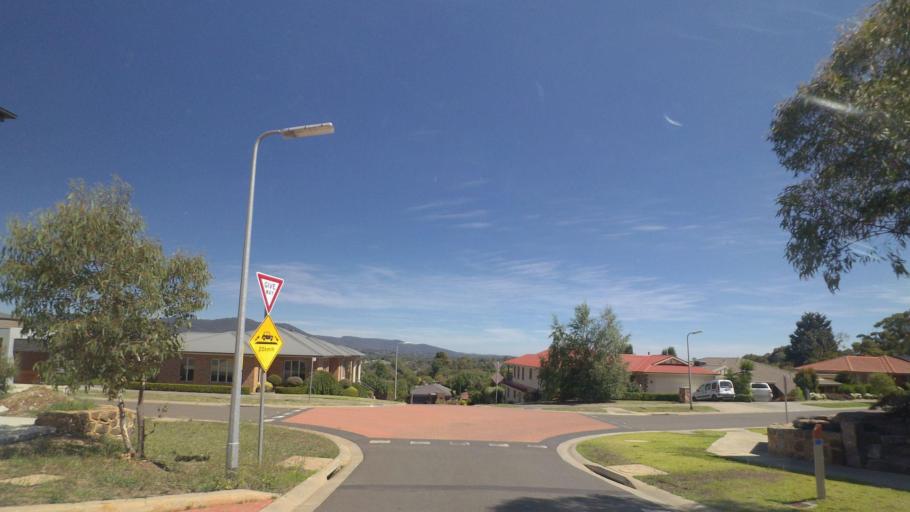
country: AU
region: Victoria
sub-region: Yarra Ranges
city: Lilydale
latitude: -37.7620
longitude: 145.3286
